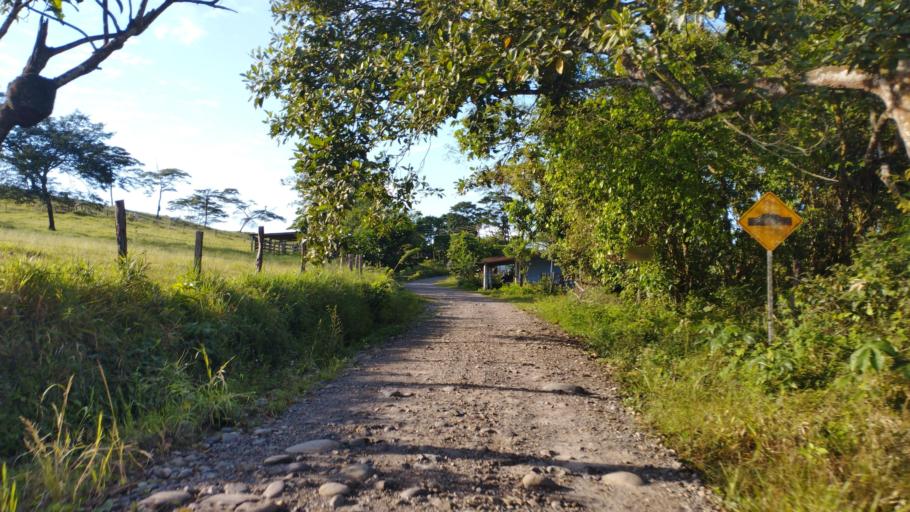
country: CO
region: Casanare
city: Sabanalarga
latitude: 4.8065
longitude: -73.0894
